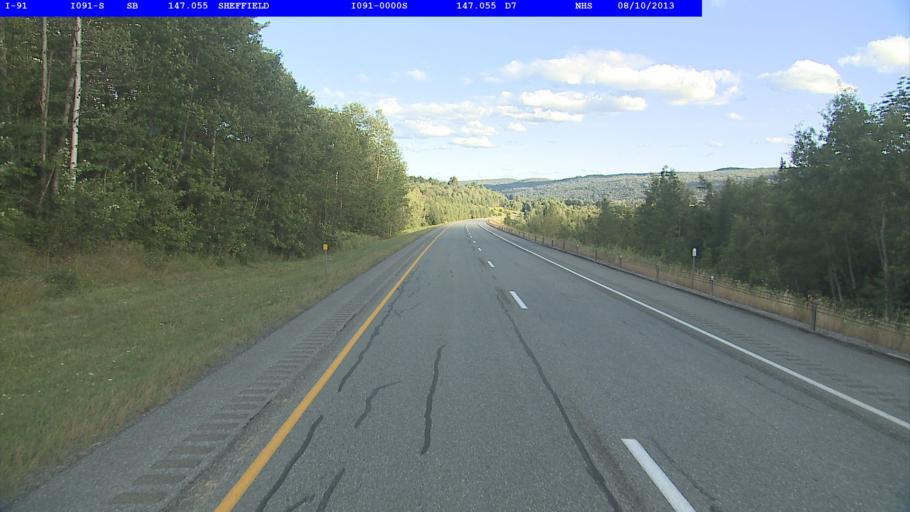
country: US
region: Vermont
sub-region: Caledonia County
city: Lyndonville
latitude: 44.6229
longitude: -72.1254
